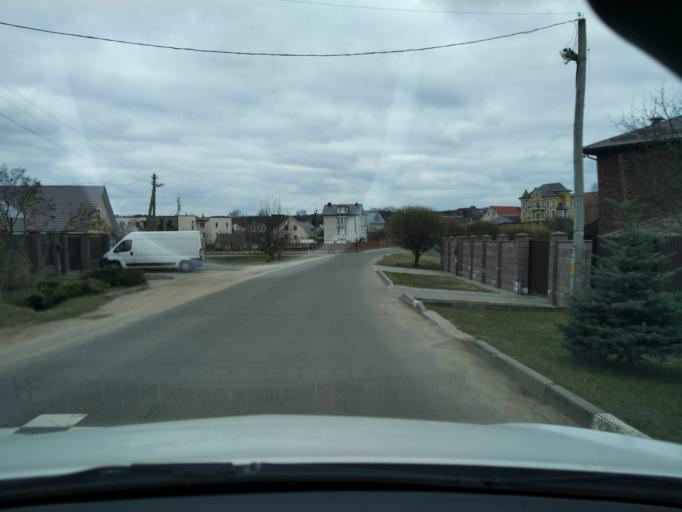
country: BY
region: Minsk
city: Bal'shavik
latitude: 53.9680
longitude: 27.5900
